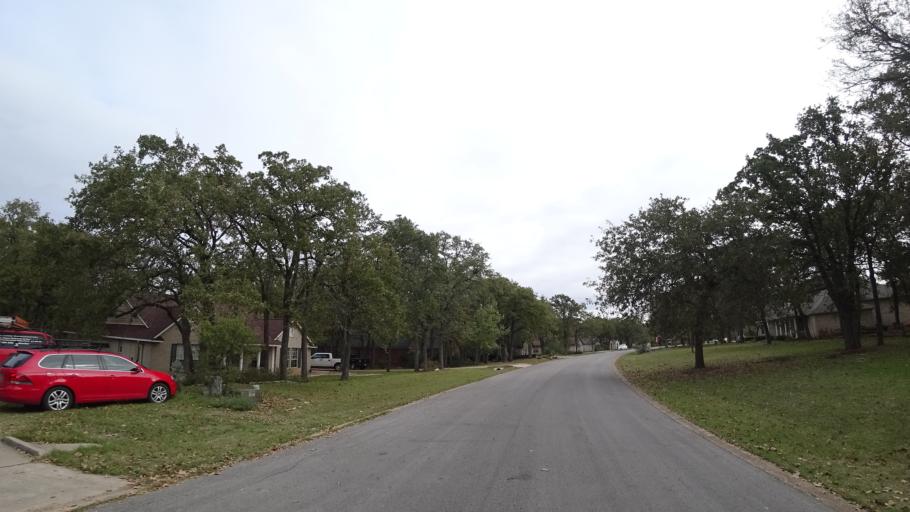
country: US
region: Texas
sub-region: Travis County
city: Shady Hollow
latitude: 30.1437
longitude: -97.8807
